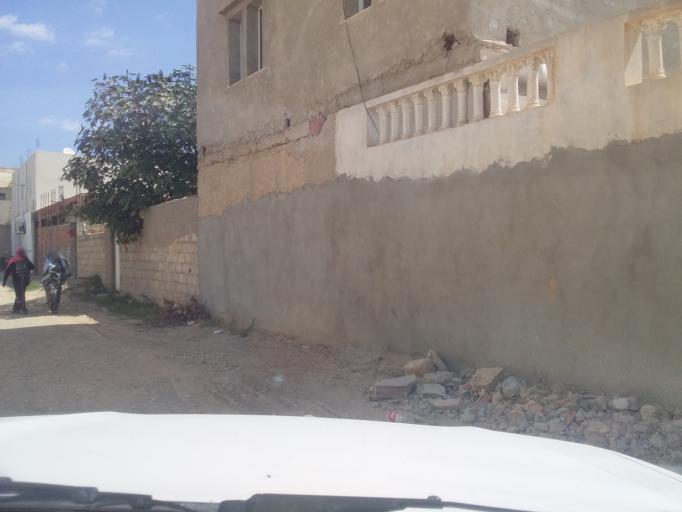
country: TN
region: Qabis
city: Matmata
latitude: 33.6144
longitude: 10.2896
